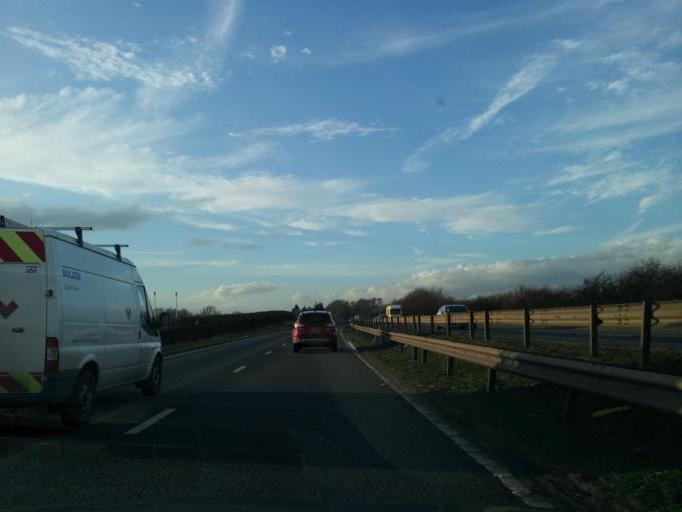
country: GB
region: England
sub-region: Peterborough
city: Wittering
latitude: 52.6176
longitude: -0.4500
